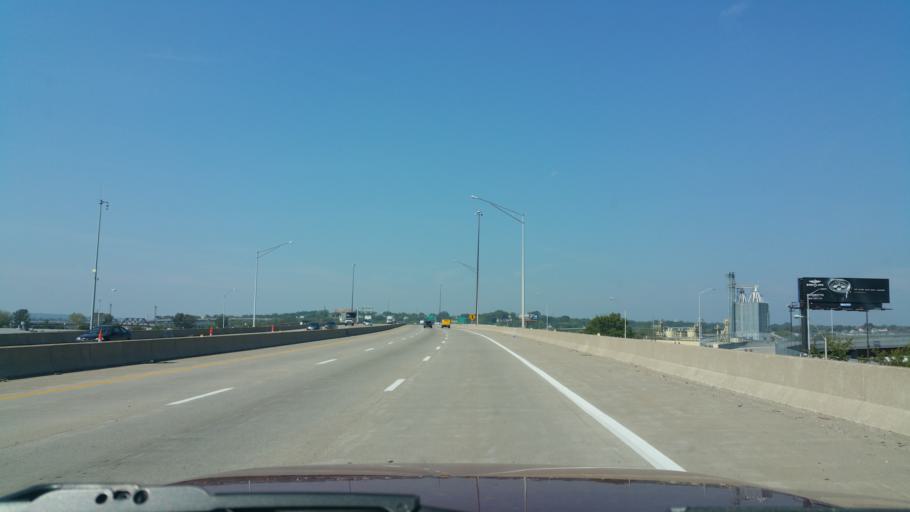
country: US
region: Missouri
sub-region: Jackson County
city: Kansas City
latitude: 39.0989
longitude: -94.6048
